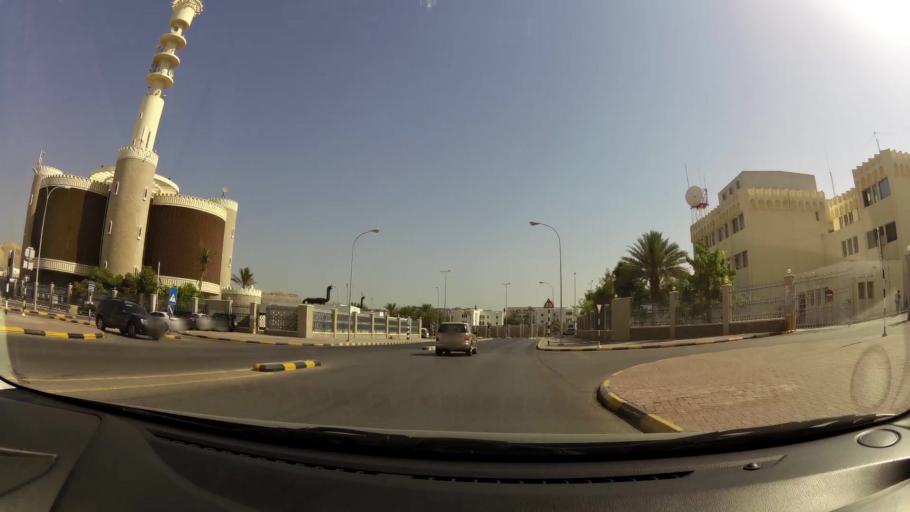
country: OM
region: Muhafazat Masqat
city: Muscat
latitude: 23.6036
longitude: 58.5464
